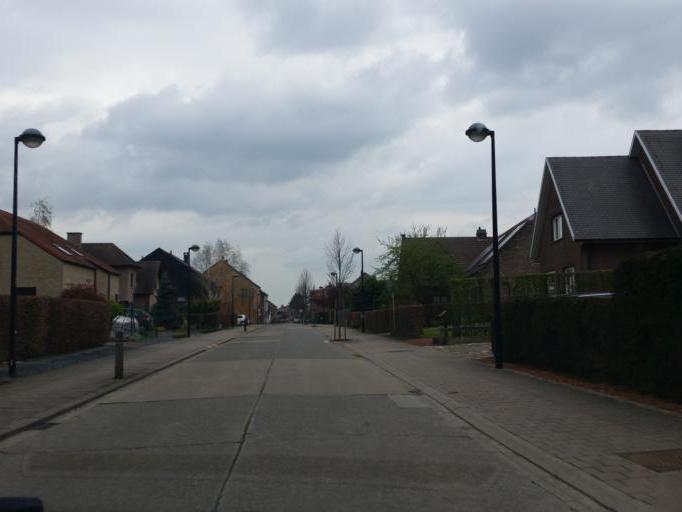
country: BE
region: Flanders
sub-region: Provincie Vlaams-Brabant
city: Kortenberg
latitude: 50.9001
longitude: 4.5778
